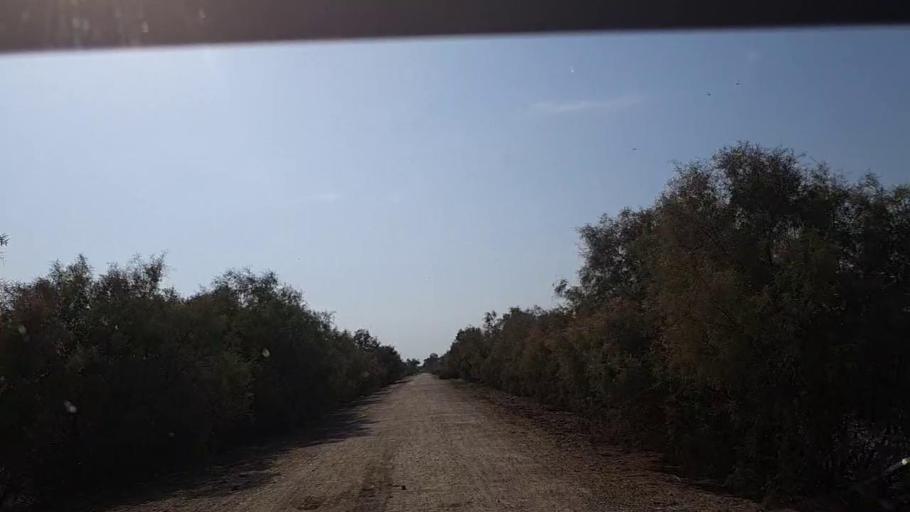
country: PK
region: Sindh
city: Khanpur
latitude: 27.8391
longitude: 69.3163
